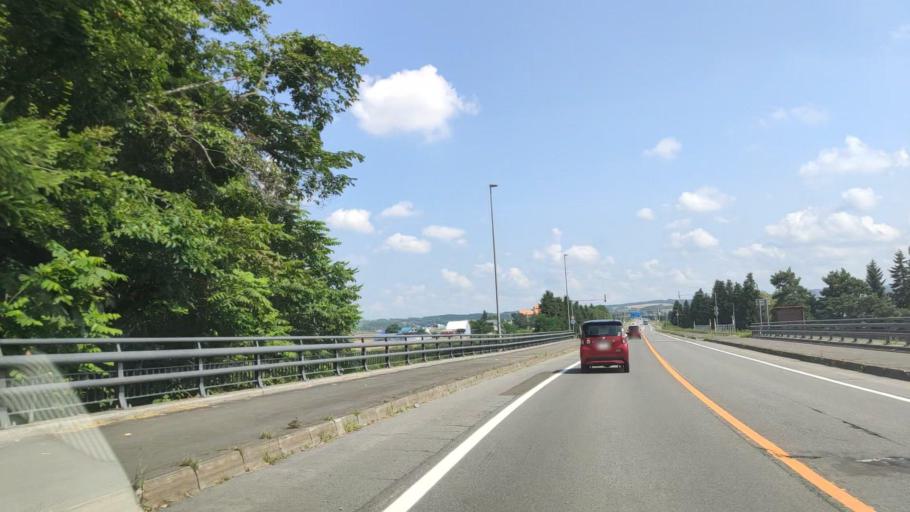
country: JP
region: Hokkaido
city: Shimo-furano
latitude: 43.4724
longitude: 142.4533
